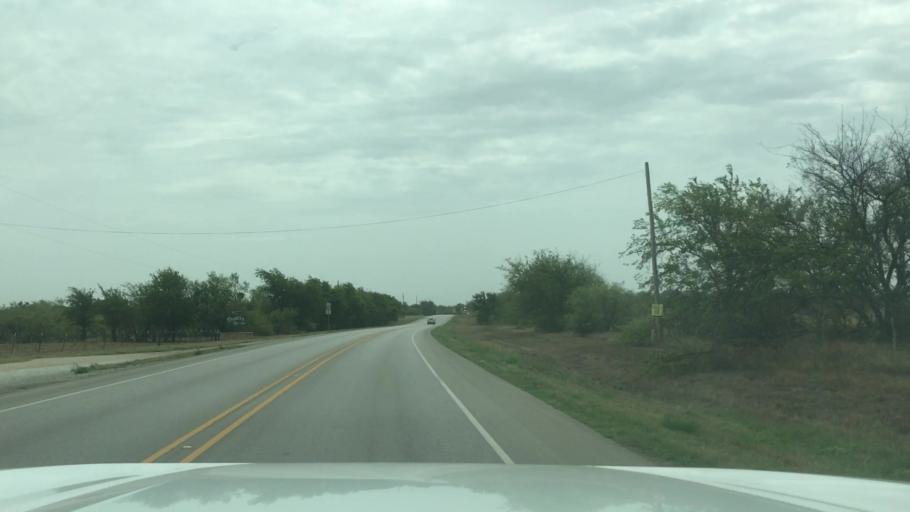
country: US
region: Texas
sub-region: Erath County
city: Dublin
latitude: 32.0918
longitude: -98.3640
